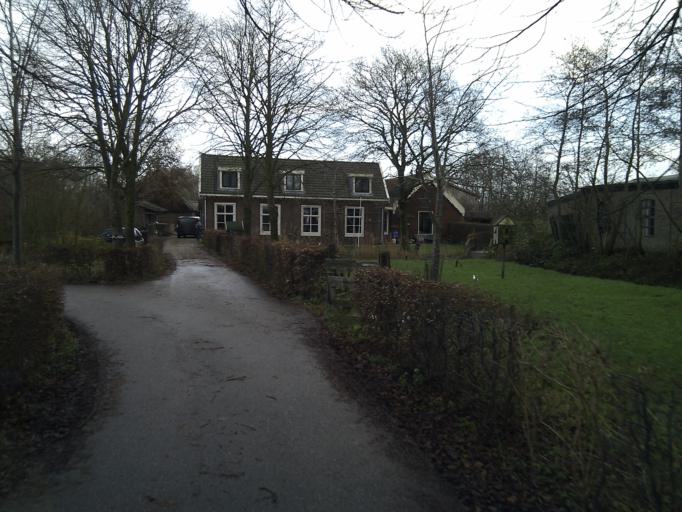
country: NL
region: Utrecht
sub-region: Stichtse Vecht
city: Vreeland
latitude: 52.2564
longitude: 4.9925
